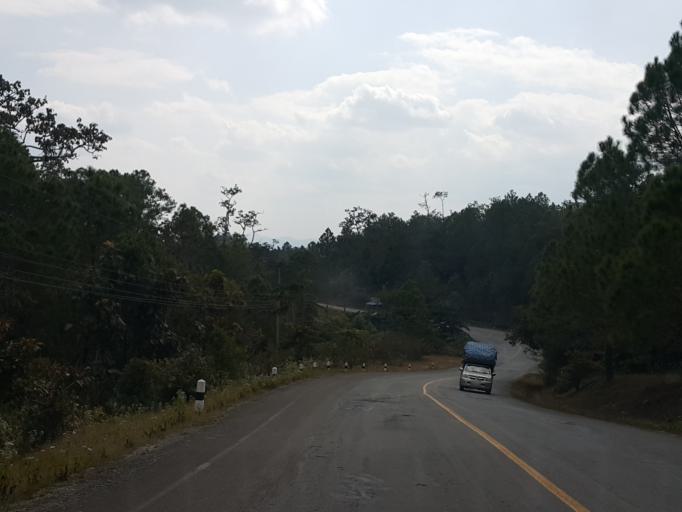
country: TH
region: Chiang Mai
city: Om Koi
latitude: 17.8535
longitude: 98.3711
